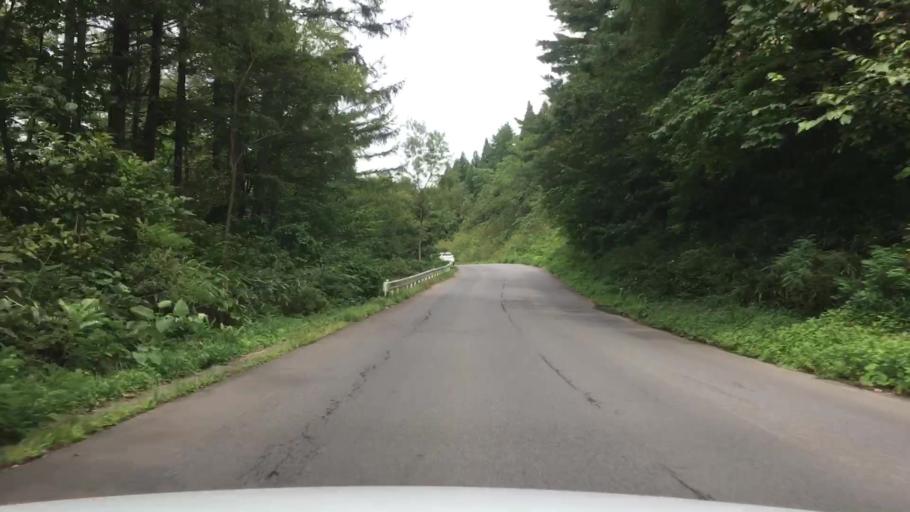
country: JP
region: Aomori
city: Shimokizukuri
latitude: 40.7186
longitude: 140.2591
